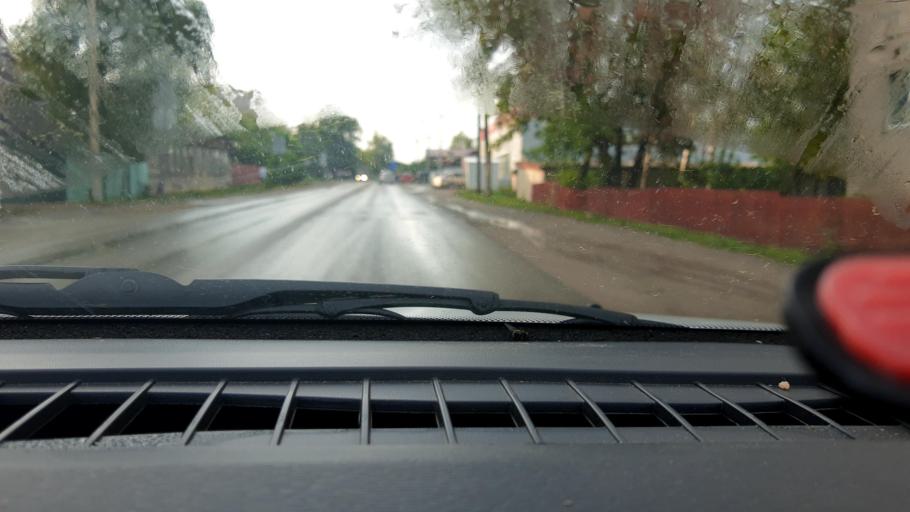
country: RU
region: Nizjnij Novgorod
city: Lukoyanov
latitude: 55.0358
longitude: 44.4945
